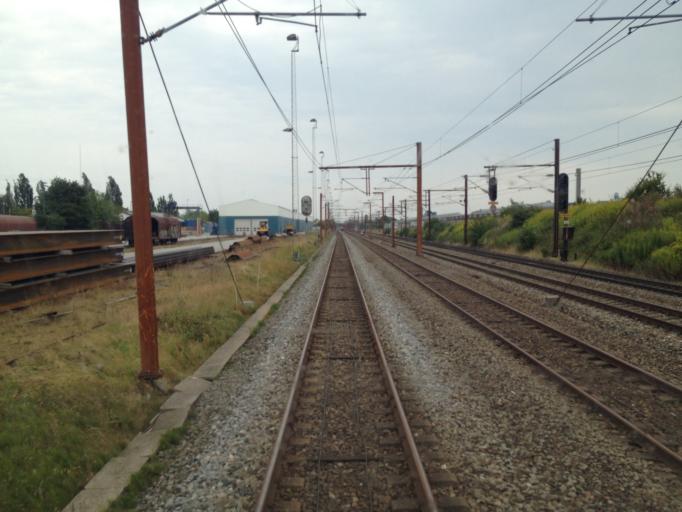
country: DK
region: Capital Region
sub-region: Albertslund Kommune
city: Albertslund
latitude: 55.6609
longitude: 12.3777
